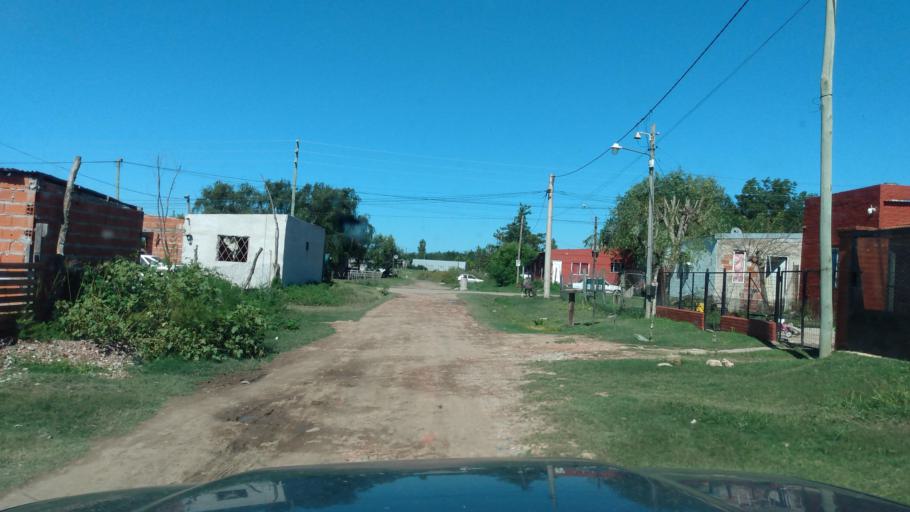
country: AR
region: Buenos Aires
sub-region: Partido de Lujan
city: Lujan
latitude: -34.5816
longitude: -59.1289
